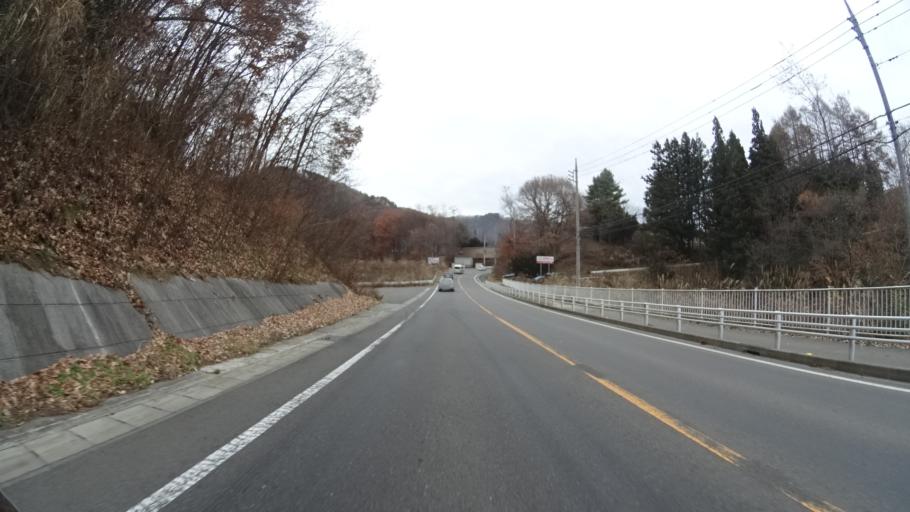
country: JP
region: Gunma
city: Numata
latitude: 36.6692
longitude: 139.1892
